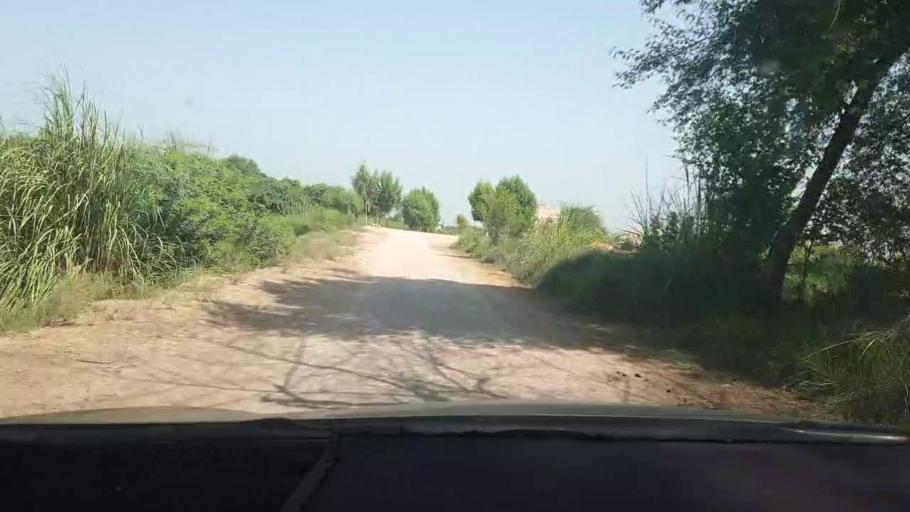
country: PK
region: Sindh
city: Miro Khan
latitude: 27.7027
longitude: 68.0872
